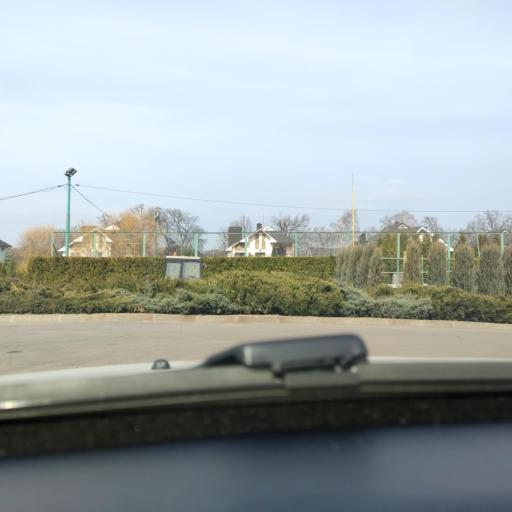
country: RU
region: Voronezj
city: Ramon'
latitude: 51.8891
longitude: 39.3585
